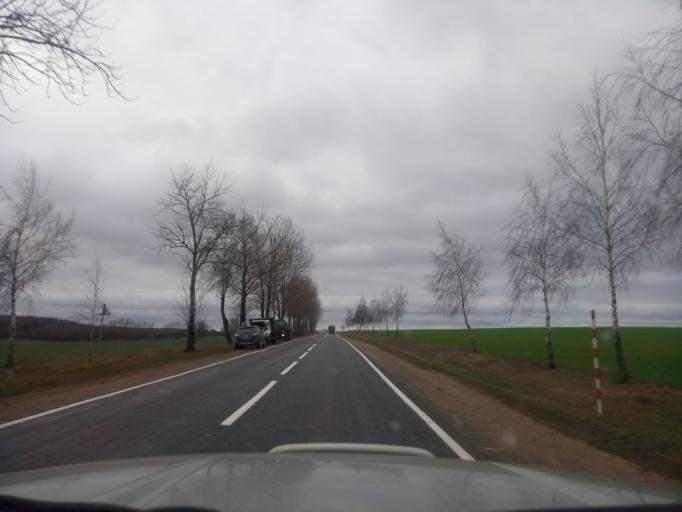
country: BY
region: Minsk
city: Kapyl'
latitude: 53.1819
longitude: 27.1745
